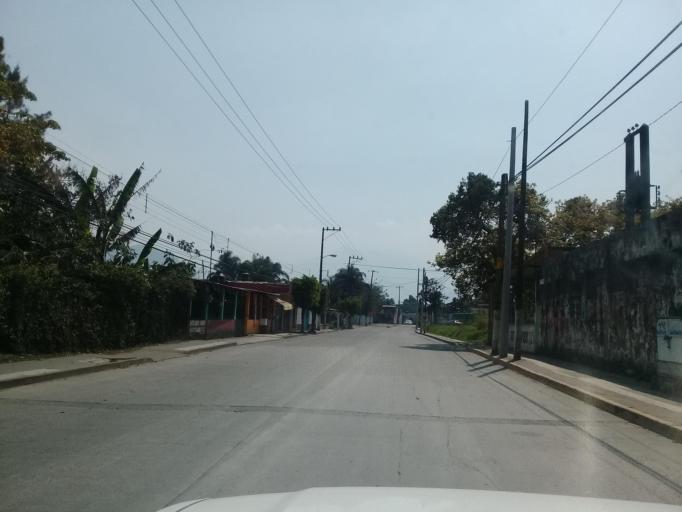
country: MX
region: Veracruz
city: Ixtac Zoquitlan
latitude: 18.8710
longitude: -97.0586
